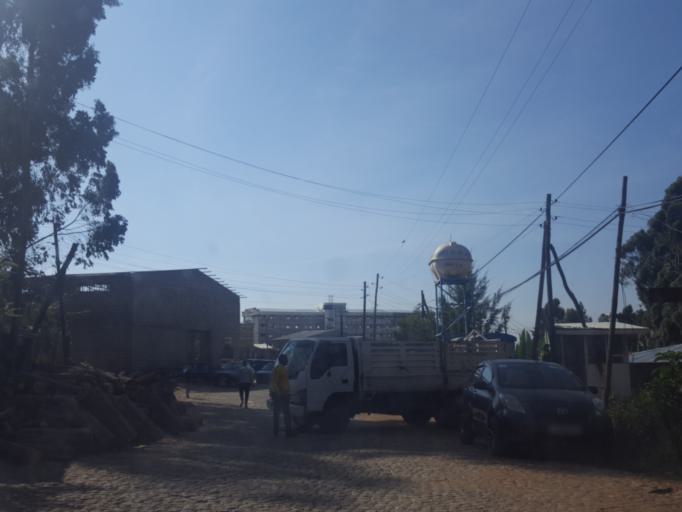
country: ET
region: Adis Abeba
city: Addis Ababa
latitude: 9.0604
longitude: 38.7133
